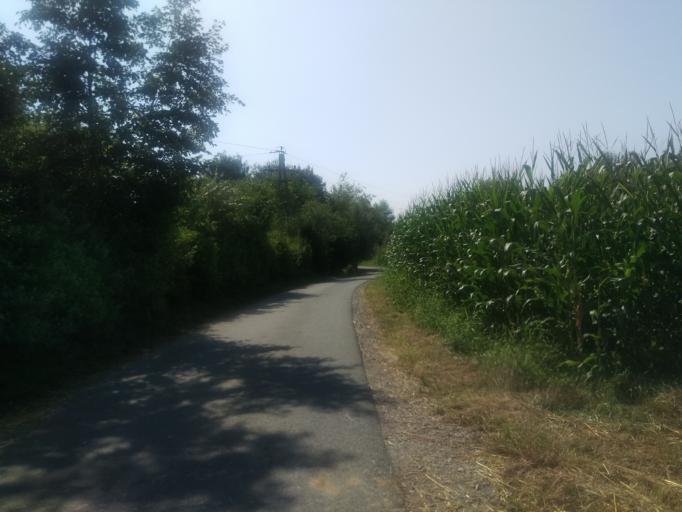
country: AT
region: Styria
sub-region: Politischer Bezirk Graz-Umgebung
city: Fernitz
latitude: 46.9753
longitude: 15.4944
